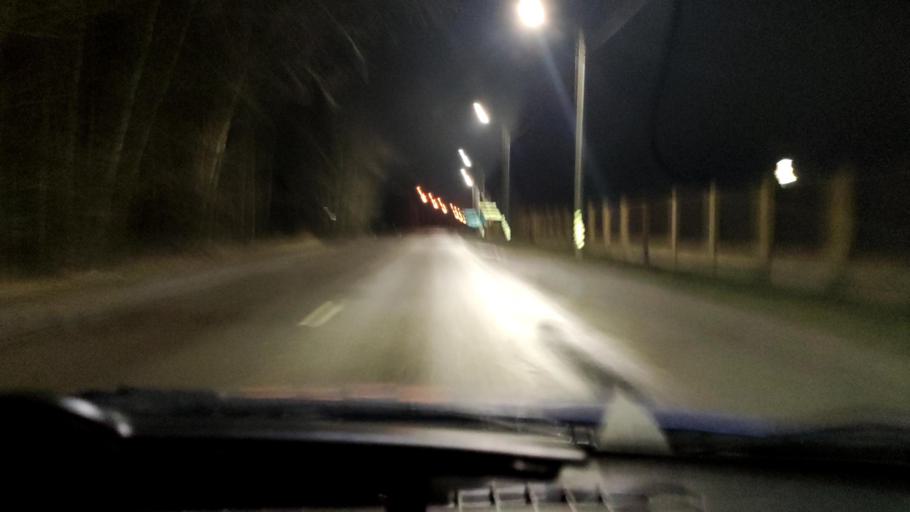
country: RU
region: Voronezj
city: Semiluki
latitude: 51.7468
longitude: 39.0483
